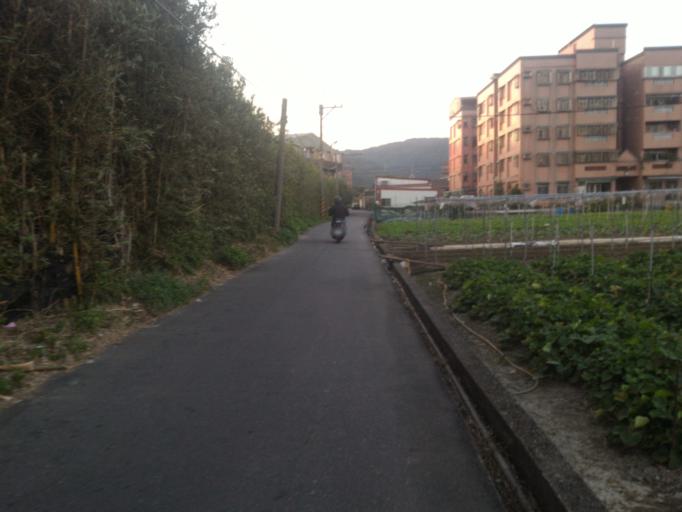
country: TW
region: Taiwan
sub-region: Taoyuan
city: Taoyuan
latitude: 24.9531
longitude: 121.3827
